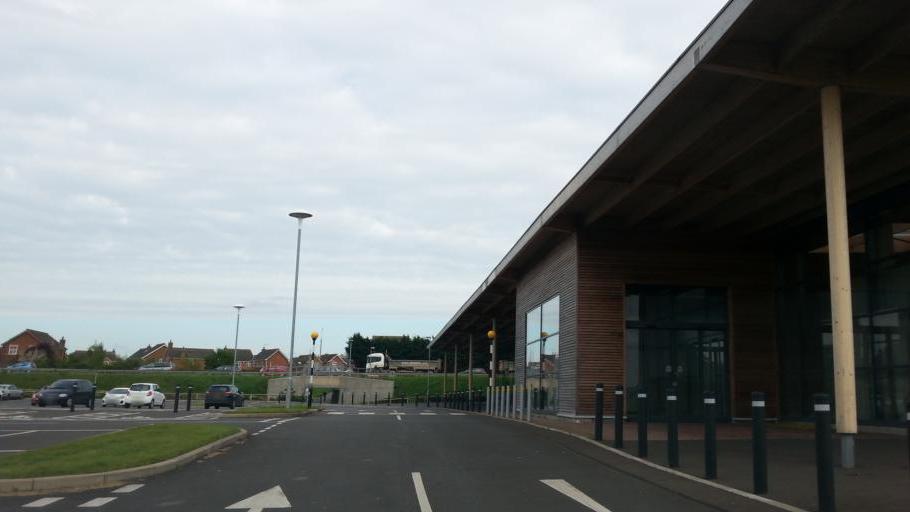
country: GB
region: England
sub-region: Cambridgeshire
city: Chatteris
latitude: 52.4581
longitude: 0.0406
